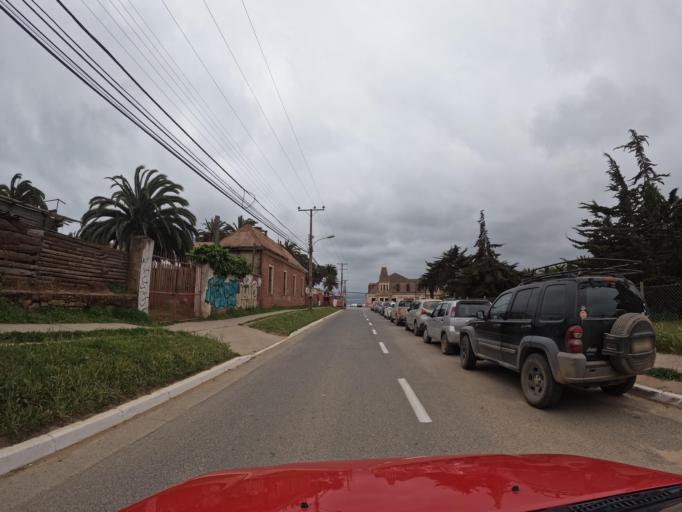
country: CL
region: O'Higgins
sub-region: Provincia de Colchagua
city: Santa Cruz
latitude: -34.3874
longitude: -72.0104
